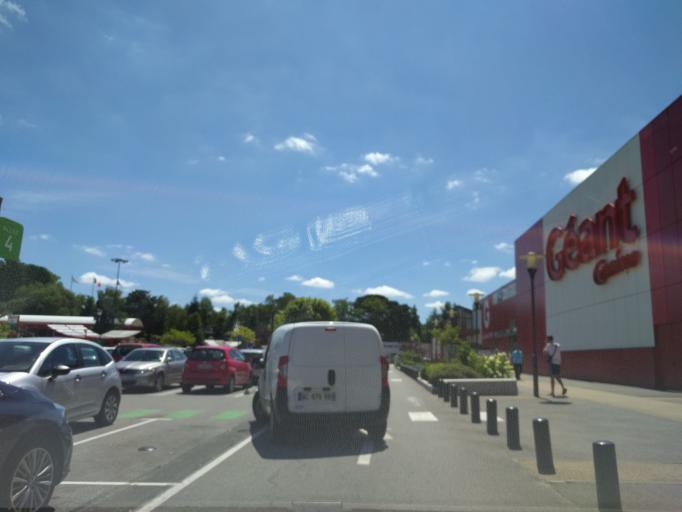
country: FR
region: Brittany
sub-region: Departement du Finistere
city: Quimper
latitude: 47.9752
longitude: -4.0939
